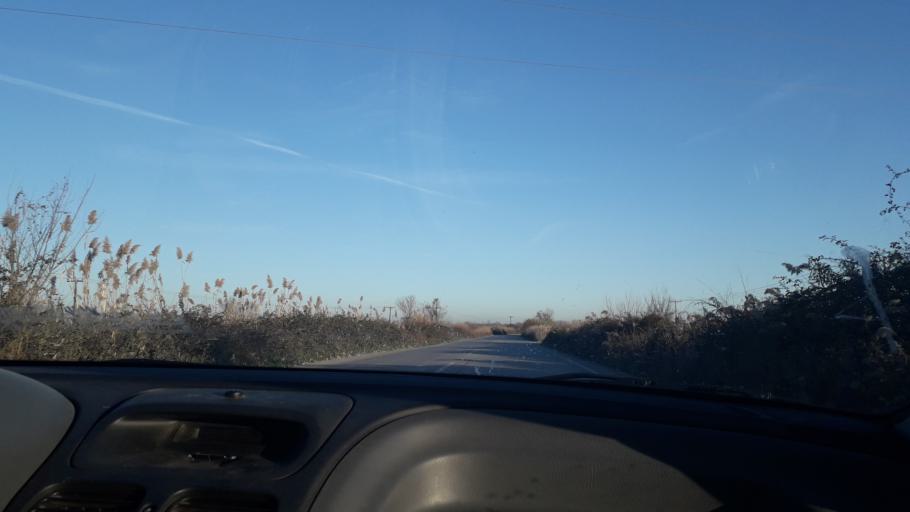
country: GR
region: Central Macedonia
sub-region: Nomos Imathias
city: Agkathia
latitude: 40.5784
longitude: 22.4752
